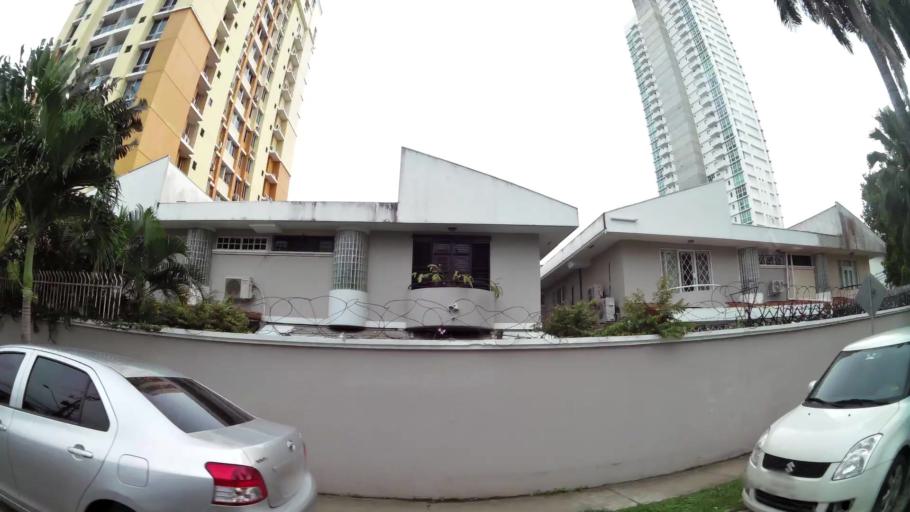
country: PA
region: Panama
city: Panama
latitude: 9.0045
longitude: -79.5055
